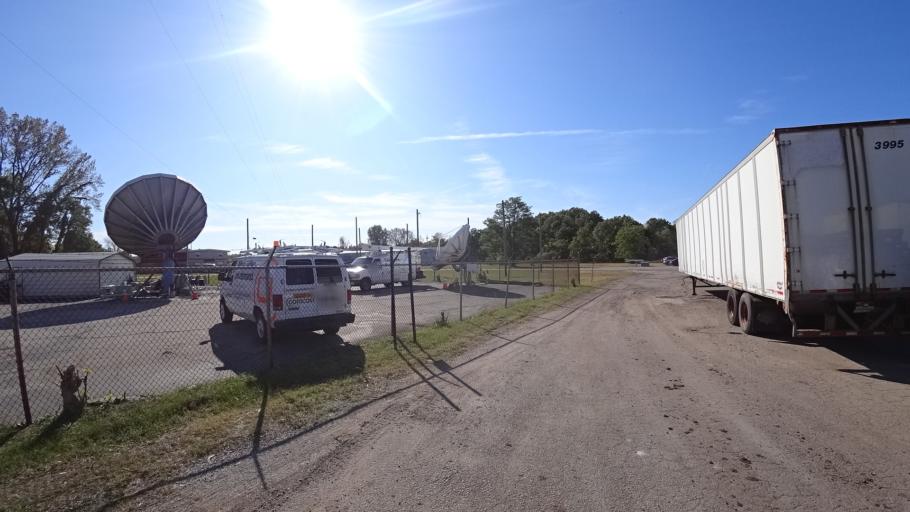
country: US
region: Indiana
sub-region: LaPorte County
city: Michigan City
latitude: 41.7022
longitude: -86.9084
